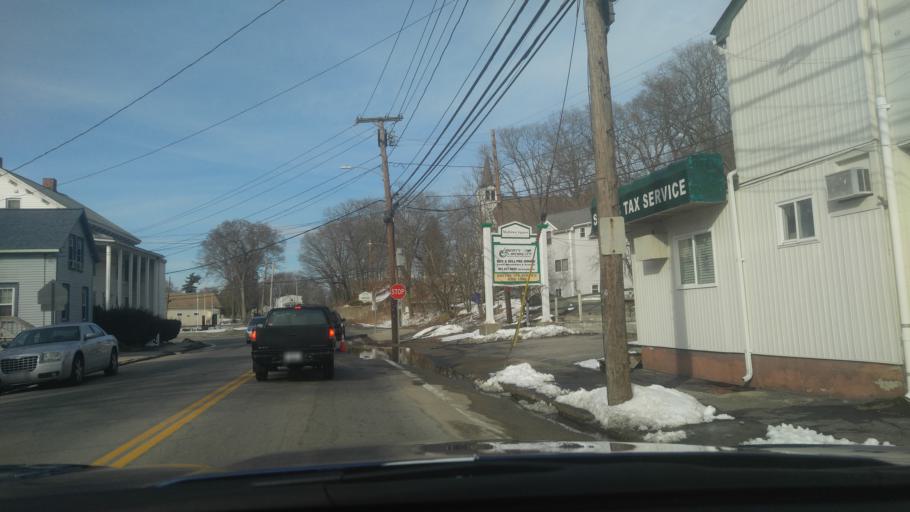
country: US
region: Rhode Island
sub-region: Kent County
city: West Warwick
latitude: 41.6916
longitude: -71.5210
